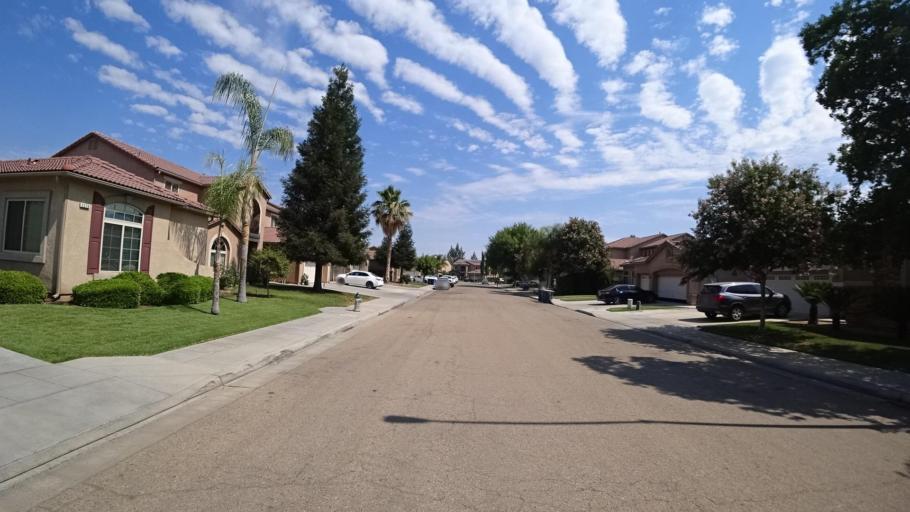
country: US
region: California
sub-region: Fresno County
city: Sunnyside
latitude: 36.7192
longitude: -119.6855
